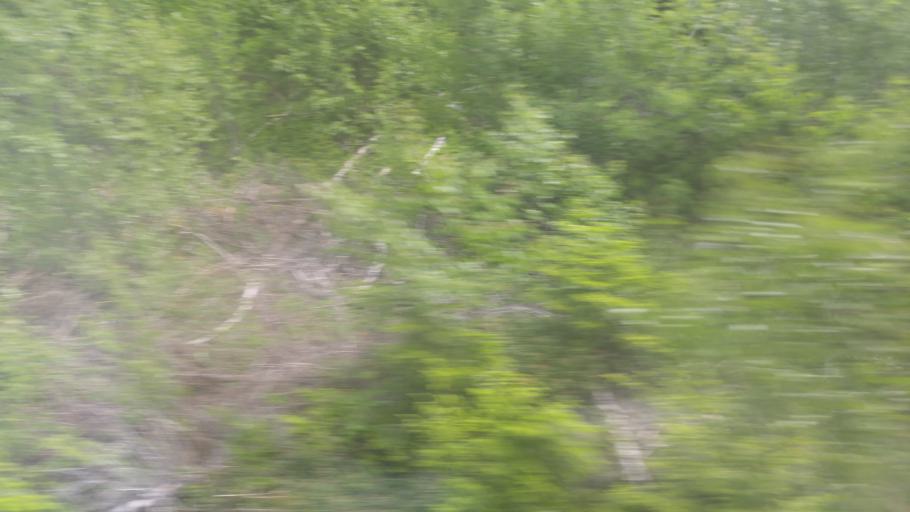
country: NO
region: Sor-Trondelag
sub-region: Selbu
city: Mebonden
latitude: 62.9688
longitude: 10.9532
